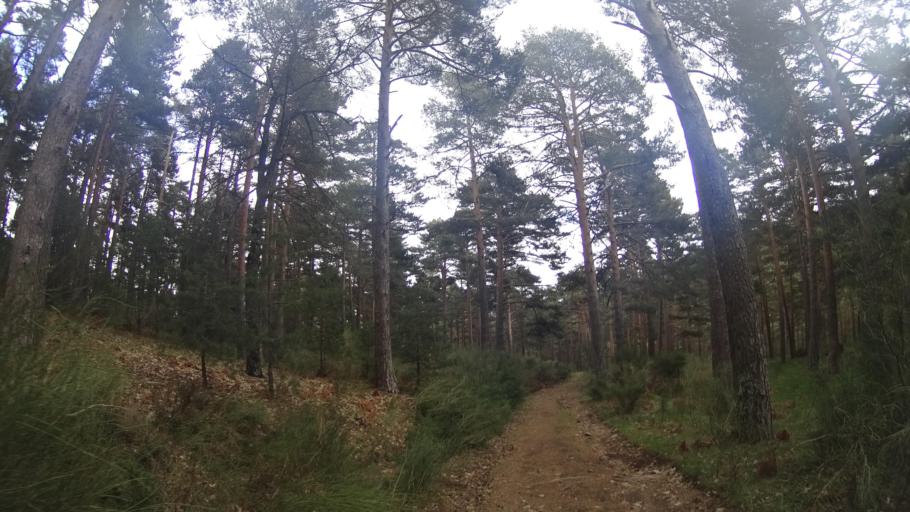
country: ES
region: Madrid
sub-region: Provincia de Madrid
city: Miraflores de la Sierra
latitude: 40.8704
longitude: -3.7878
